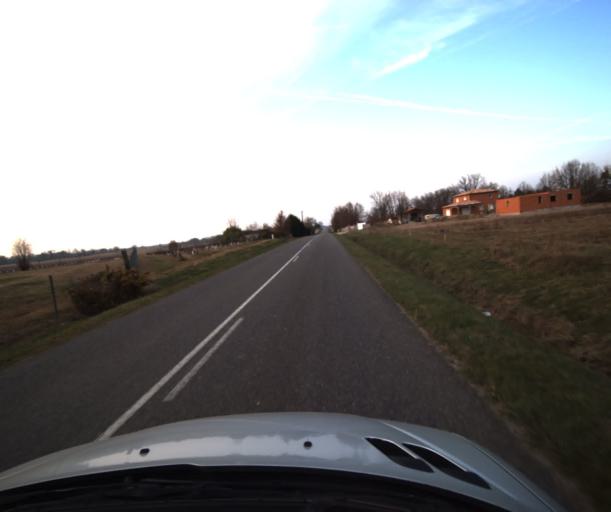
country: FR
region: Midi-Pyrenees
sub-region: Departement du Tarn-et-Garonne
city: Labastide-Saint-Pierre
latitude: 43.8849
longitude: 1.3756
